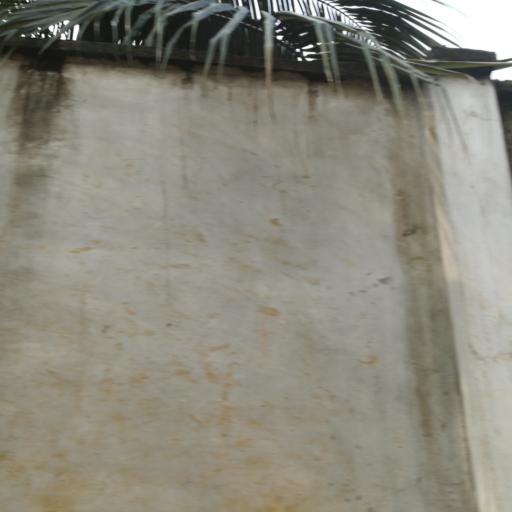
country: NG
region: Rivers
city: Port Harcourt
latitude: 4.8483
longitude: 7.0564
